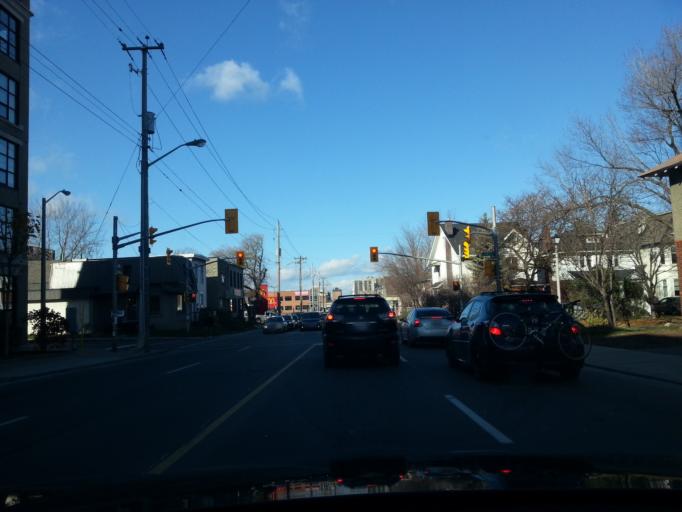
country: CA
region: Ontario
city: Ottawa
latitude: 45.4022
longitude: -75.7003
